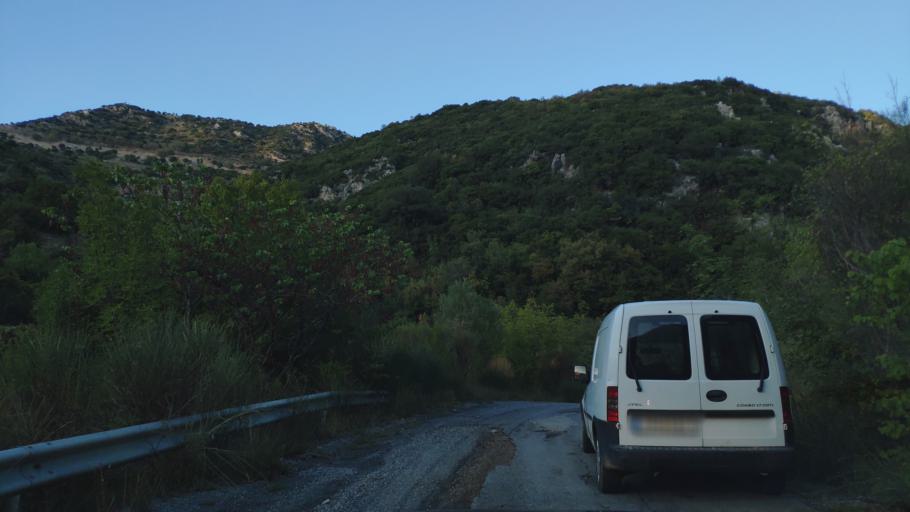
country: GR
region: Peloponnese
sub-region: Nomos Arkadias
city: Dimitsana
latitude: 37.5753
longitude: 22.0524
